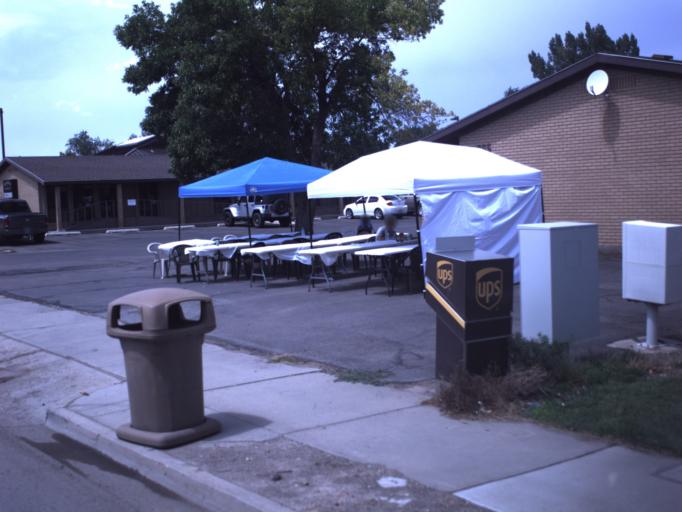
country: US
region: Utah
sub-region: Duchesne County
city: Roosevelt
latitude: 40.3022
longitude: -109.9781
